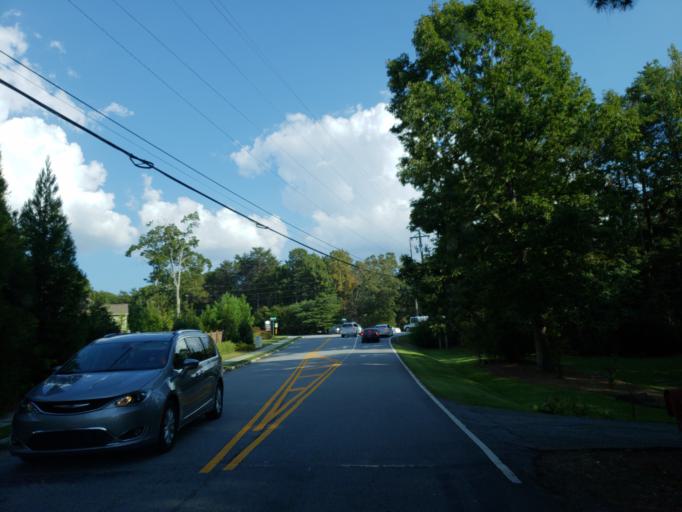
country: US
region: Georgia
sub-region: Fulton County
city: Roswell
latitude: 34.0589
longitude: -84.4387
